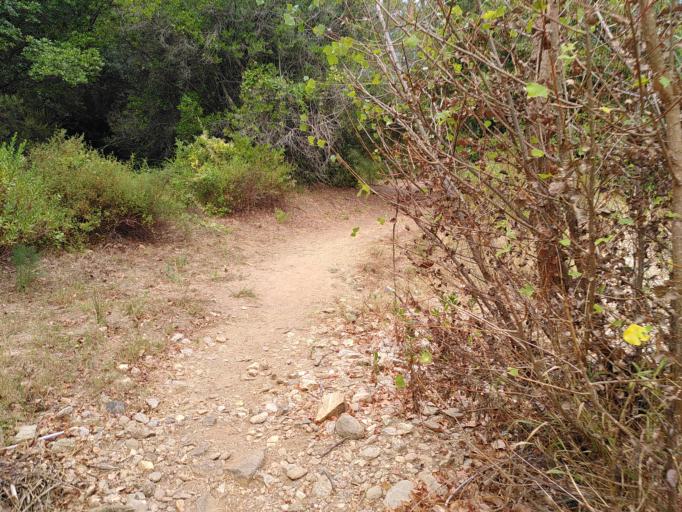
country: FR
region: Provence-Alpes-Cote d'Azur
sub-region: Departement du Var
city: Cavalaire-sur-Mer
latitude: 43.1654
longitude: 6.5178
